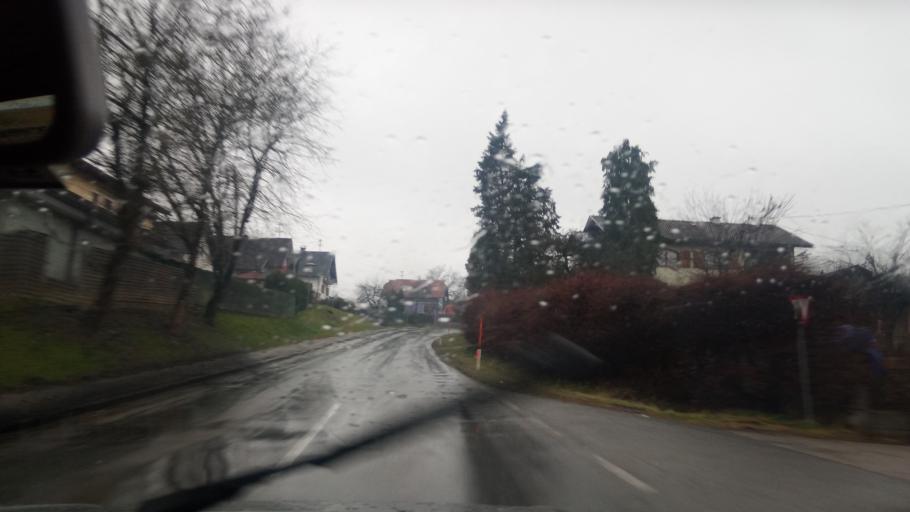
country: AT
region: Carinthia
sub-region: Politischer Bezirk Klagenfurt Land
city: Kottmannsdorf
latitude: 46.5875
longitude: 14.2365
